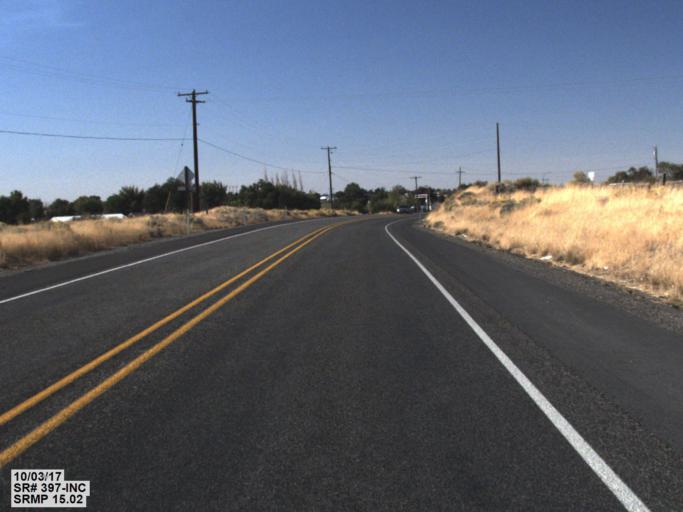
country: US
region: Washington
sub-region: Benton County
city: Finley
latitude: 46.1845
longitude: -119.0716
